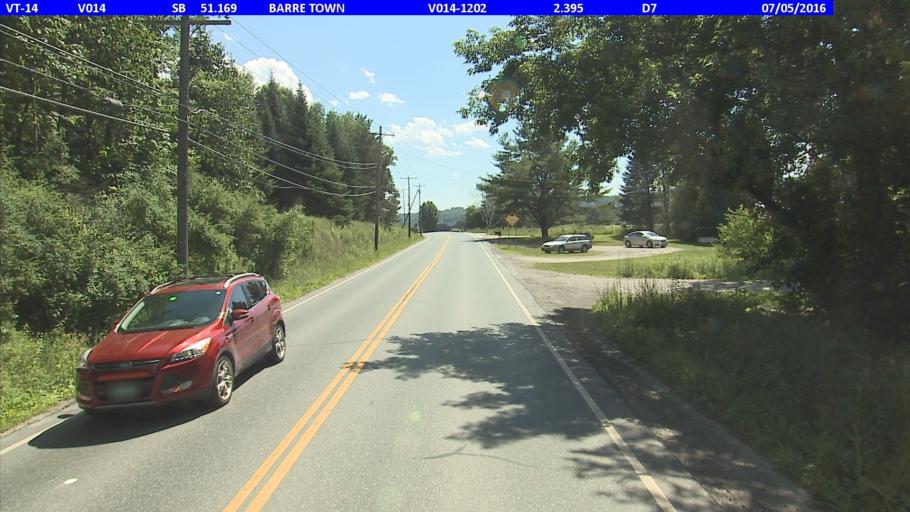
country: US
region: Vermont
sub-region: Washington County
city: Barre
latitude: 44.2143
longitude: -72.4961
